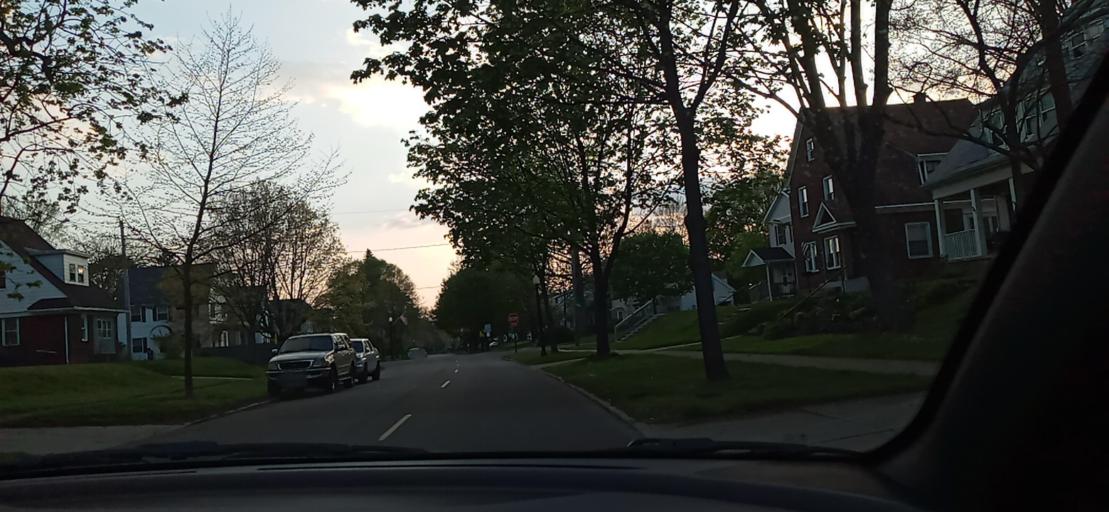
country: US
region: Ohio
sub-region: Summit County
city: Akron
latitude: 41.0446
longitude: -81.5142
